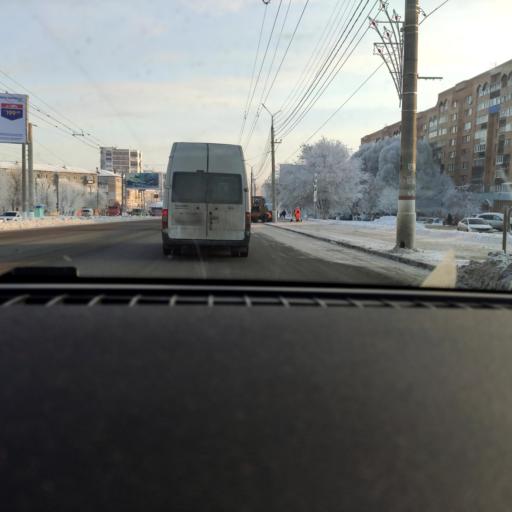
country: RU
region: Samara
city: Novokuybyshevsk
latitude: 53.0932
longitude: 49.9794
